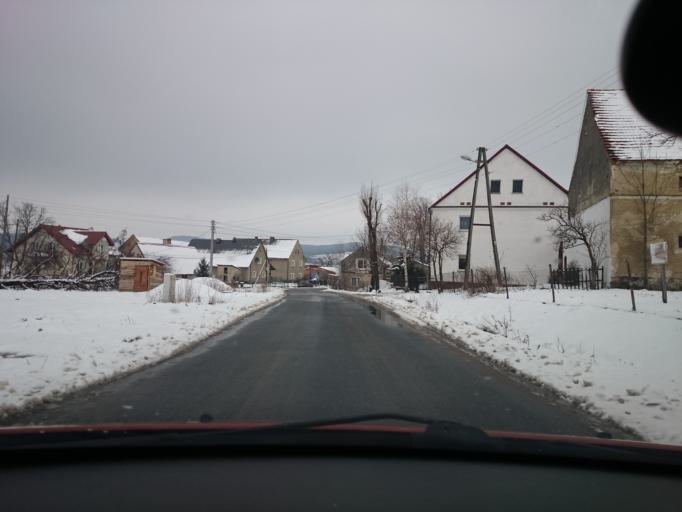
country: PL
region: Lower Silesian Voivodeship
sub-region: Powiat zabkowicki
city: Bardo
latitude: 50.5407
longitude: 16.7370
